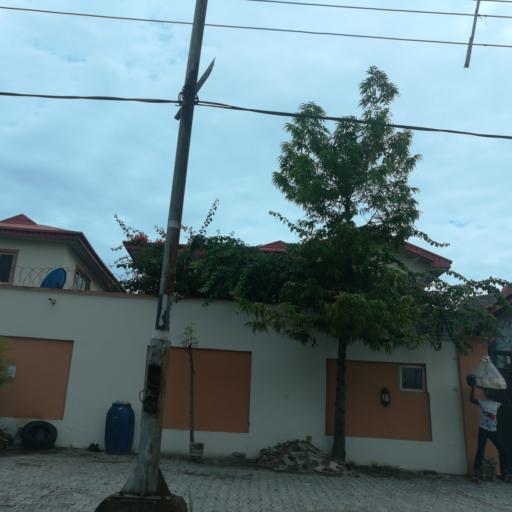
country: NG
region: Lagos
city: Ikoyi
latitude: 6.4425
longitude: 3.4772
